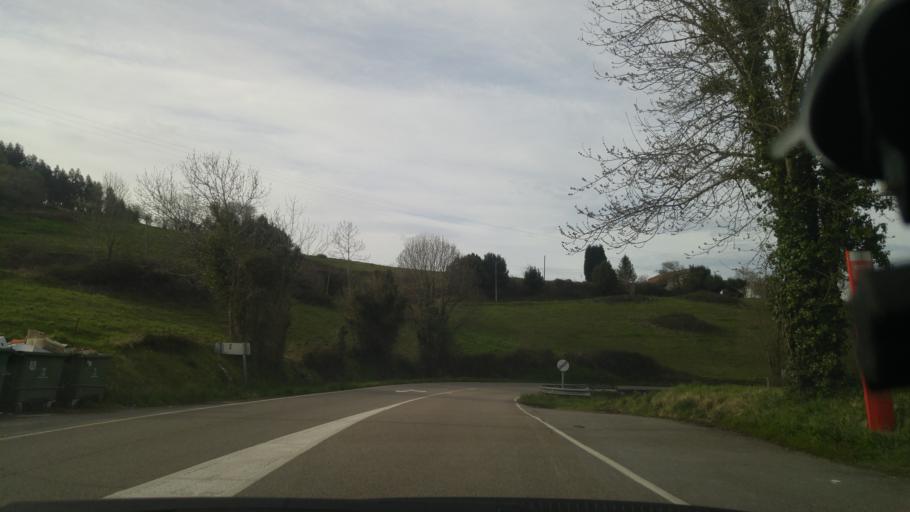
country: ES
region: Asturias
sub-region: Province of Asturias
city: Llanera
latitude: 43.4643
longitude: -5.8504
